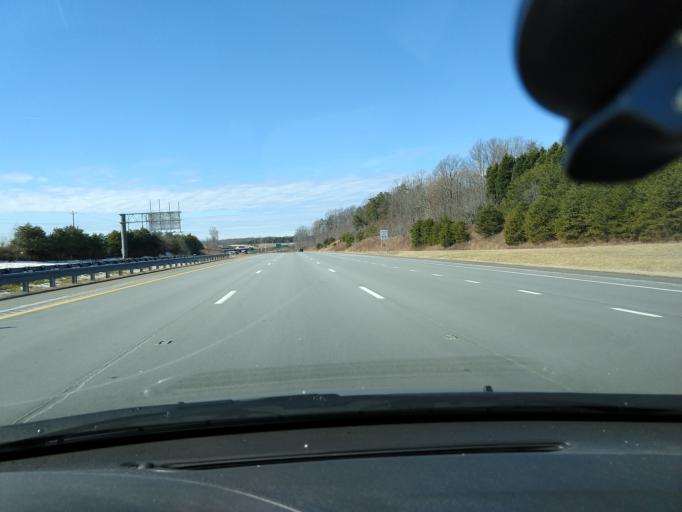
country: US
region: North Carolina
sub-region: Guilford County
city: Oak Ridge
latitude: 36.1201
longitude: -79.9180
